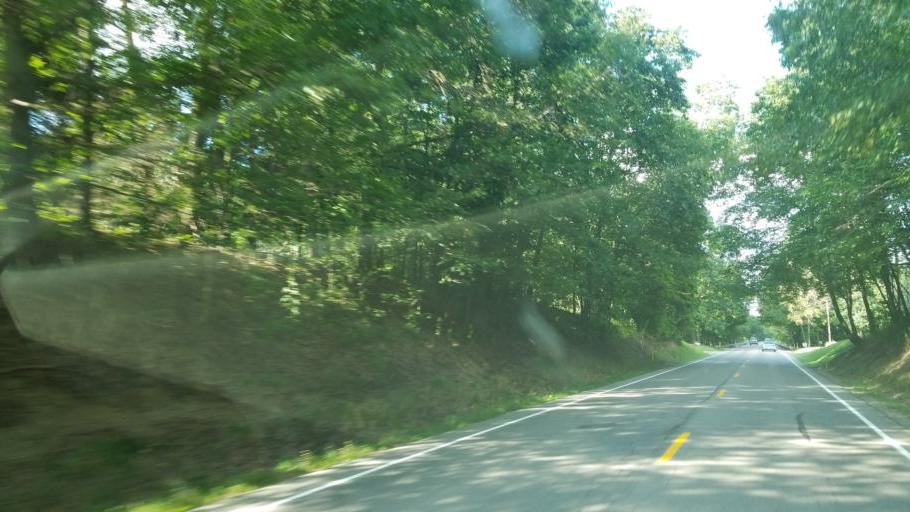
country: US
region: Pennsylvania
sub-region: Clarion County
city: Knox
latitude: 41.2189
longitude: -79.5345
